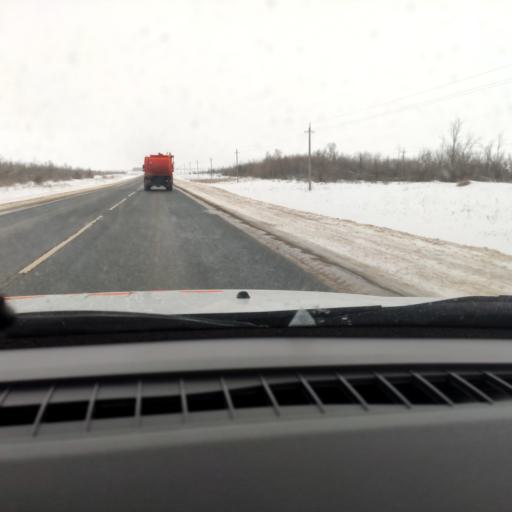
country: RU
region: Saratov
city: Perelyub
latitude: 52.1673
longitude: 50.7967
